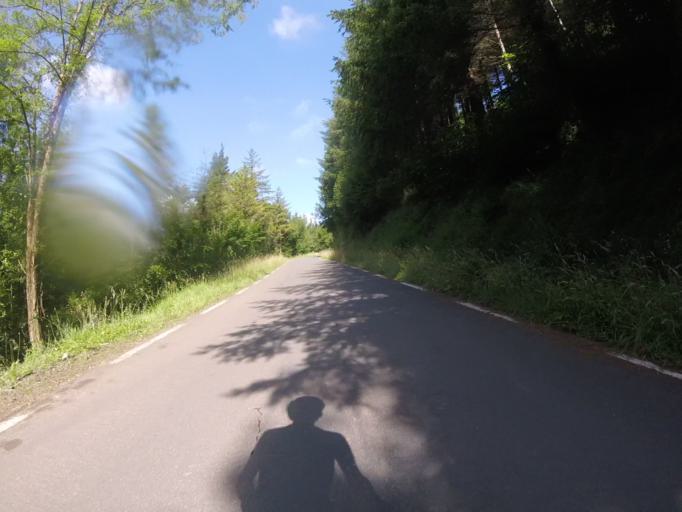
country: ES
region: Basque Country
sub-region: Provincia de Guipuzcoa
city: Beasain
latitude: 43.0811
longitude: -2.2218
